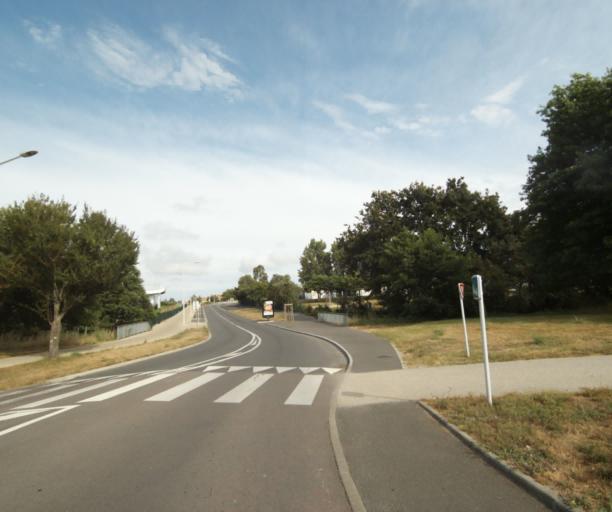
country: FR
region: Pays de la Loire
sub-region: Departement de la Vendee
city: Chateau-d'Olonne
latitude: 46.4922
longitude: -1.7458
